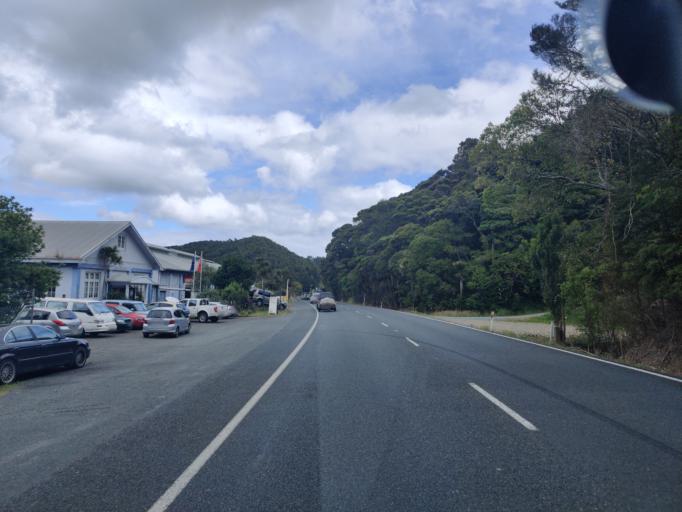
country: NZ
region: Northland
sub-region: Far North District
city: Kerikeri
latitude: -35.0932
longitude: 173.7710
